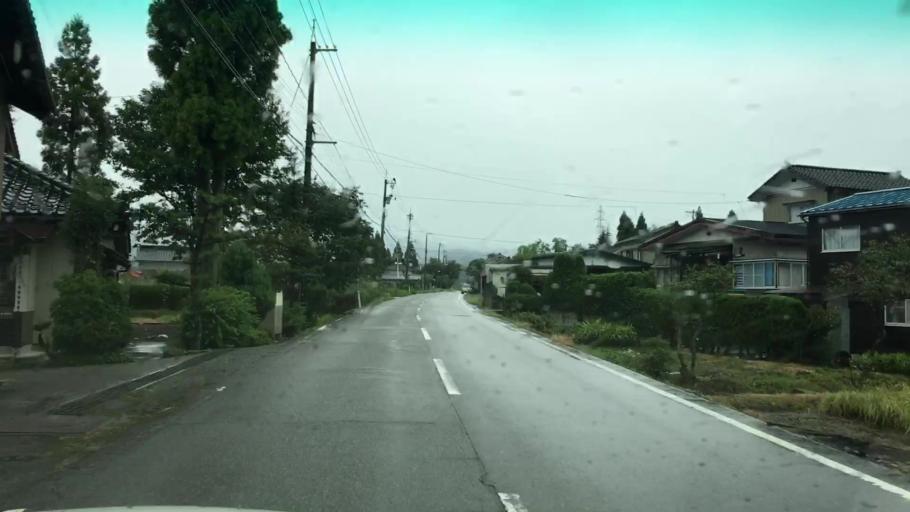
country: JP
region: Toyama
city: Kamiichi
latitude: 36.6202
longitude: 137.3230
